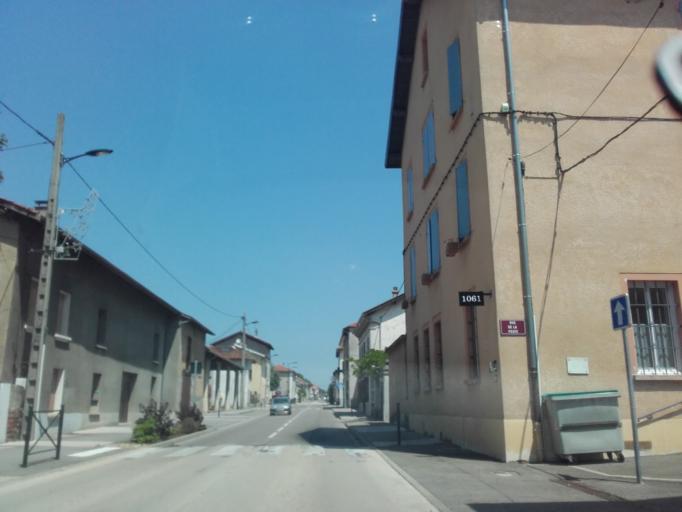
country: FR
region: Rhone-Alpes
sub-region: Departement de l'Isere
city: Champier
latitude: 45.4510
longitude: 5.2901
